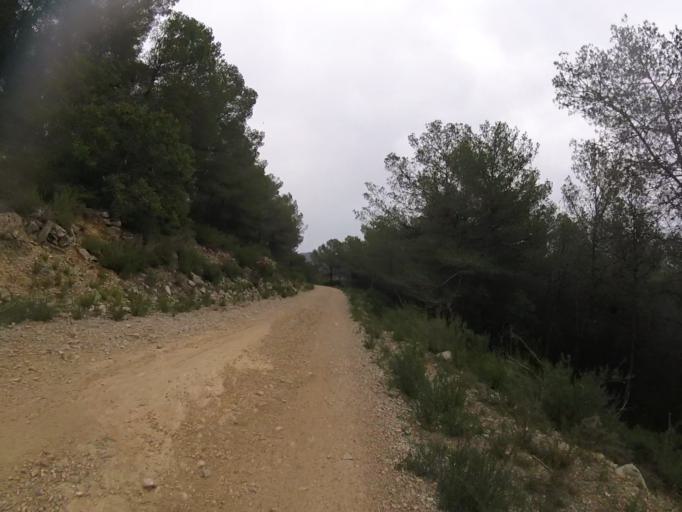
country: ES
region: Valencia
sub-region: Provincia de Castello
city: Alcala de Xivert
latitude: 40.3120
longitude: 0.2654
